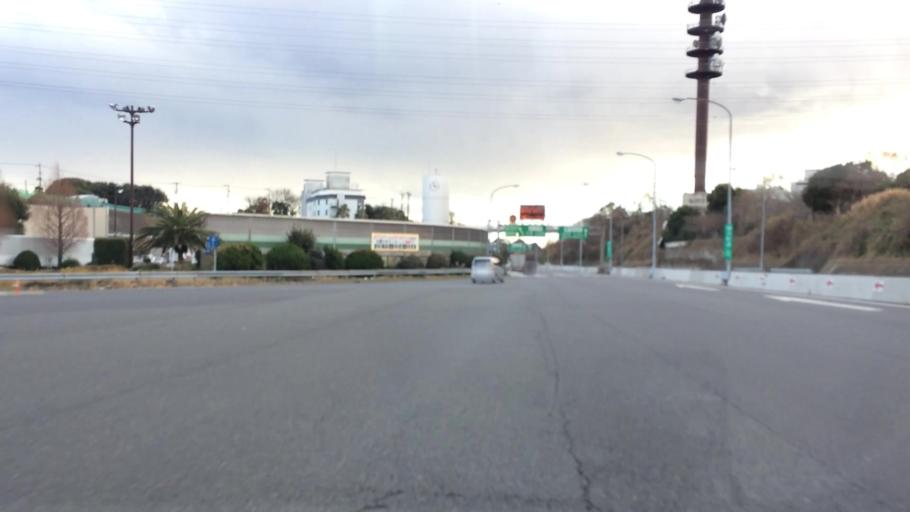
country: JP
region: Kanagawa
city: Yokohama
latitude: 35.4835
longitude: 139.5940
